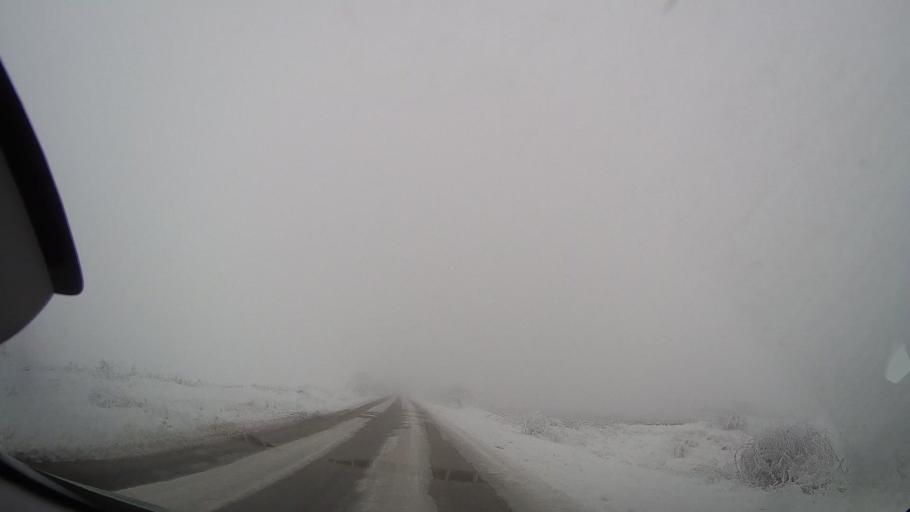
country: RO
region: Neamt
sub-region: Comuna Valea Ursului
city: Valea Ursului
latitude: 46.8232
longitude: 27.0630
